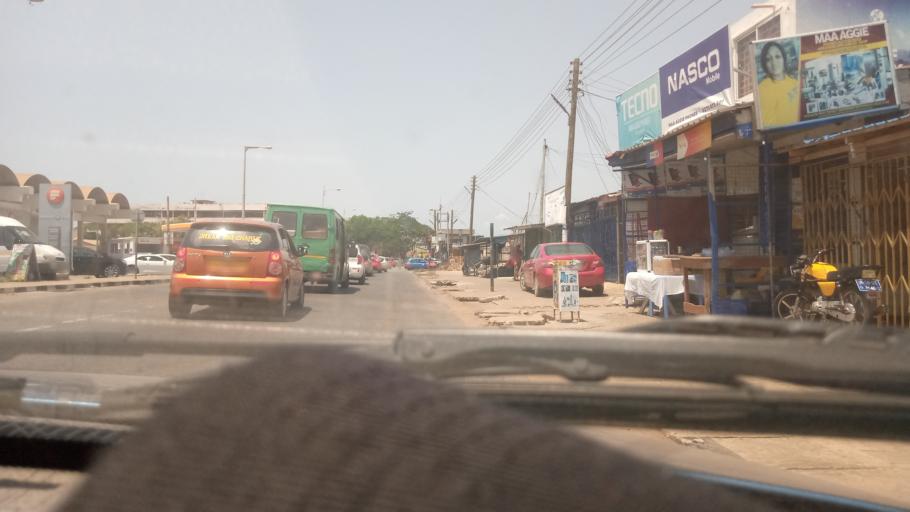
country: GH
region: Greater Accra
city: Accra
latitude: 5.5340
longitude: -0.2368
